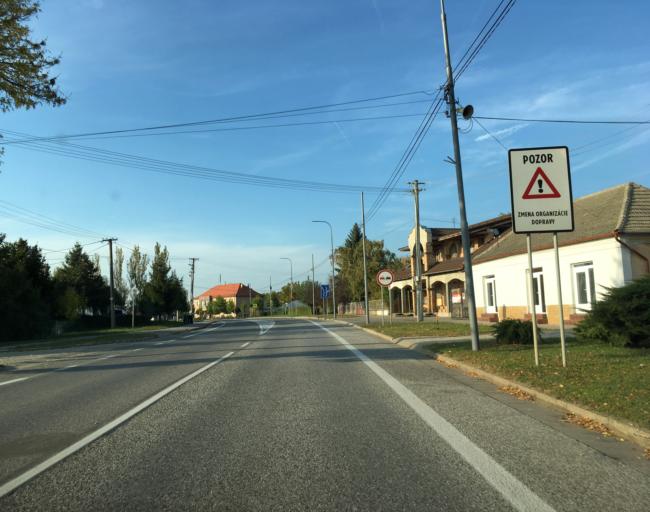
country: SK
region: Nitriansky
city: Surany
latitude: 48.0931
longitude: 18.0660
